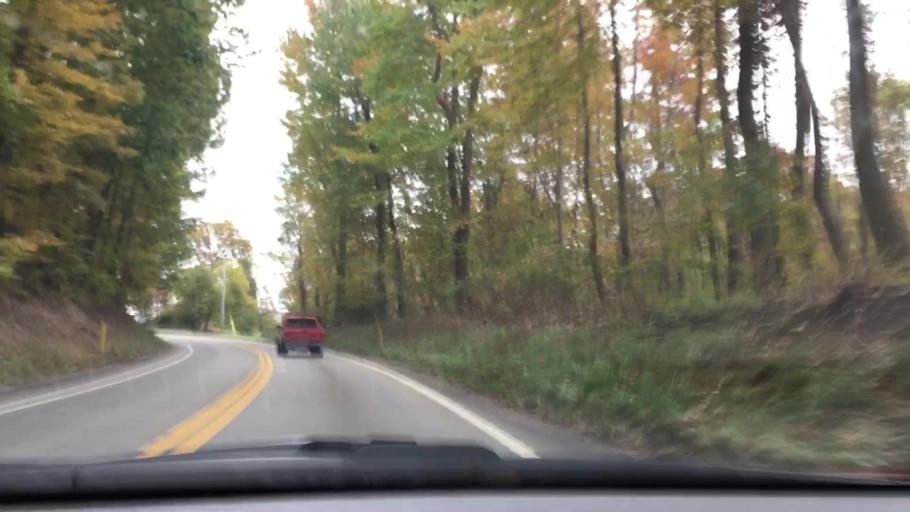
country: US
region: Pennsylvania
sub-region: Armstrong County
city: Orchard Hills
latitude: 40.6095
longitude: -79.4720
